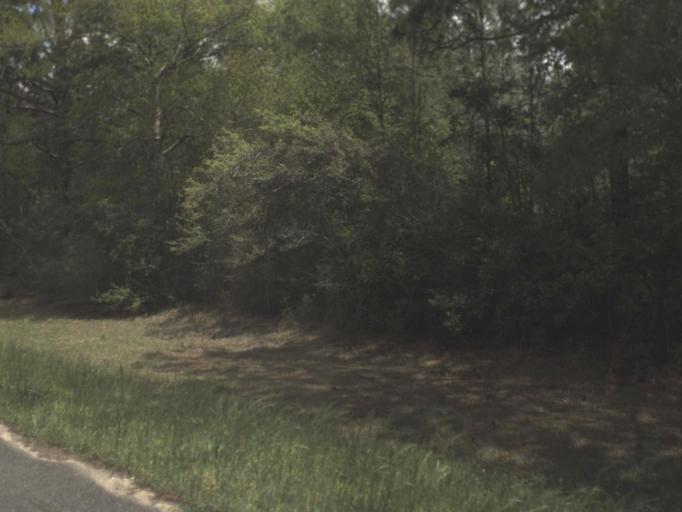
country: US
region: Florida
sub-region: Okaloosa County
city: Crestview
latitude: 30.8173
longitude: -86.6773
